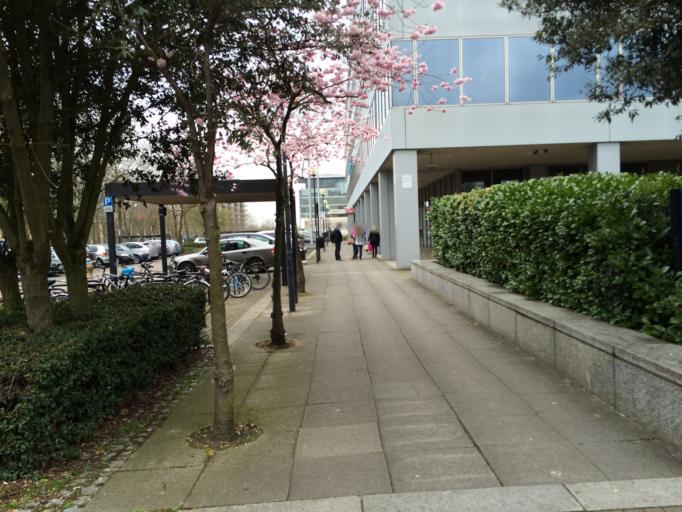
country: GB
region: England
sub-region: Milton Keynes
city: Milton Keynes
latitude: 52.0389
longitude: -0.7586
